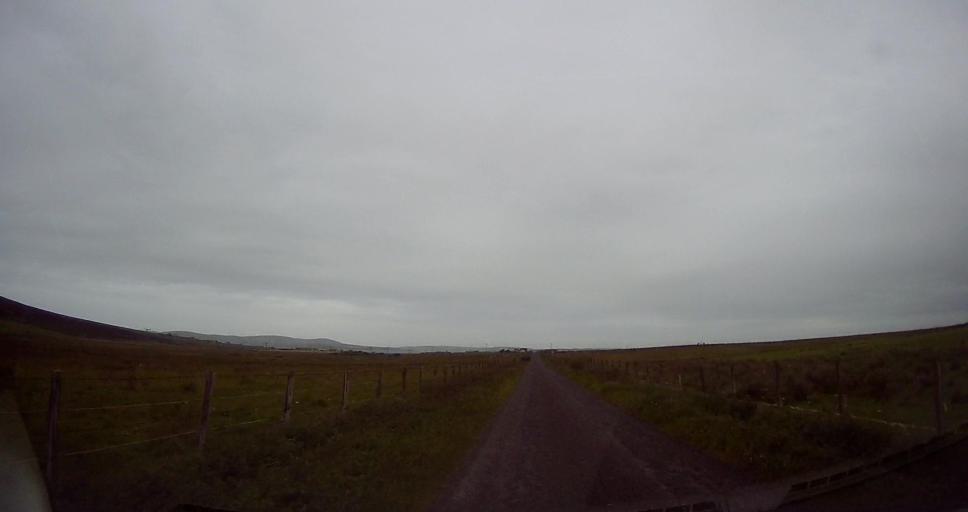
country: GB
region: Scotland
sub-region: Orkney Islands
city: Stromness
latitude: 58.9809
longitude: -3.1786
